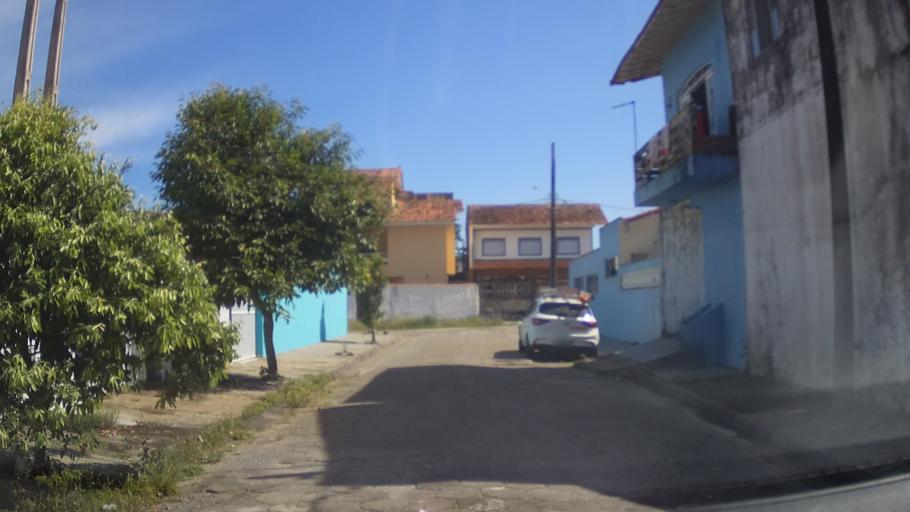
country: BR
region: Sao Paulo
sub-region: Itanhaem
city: Itanhaem
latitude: -24.1593
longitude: -46.7394
